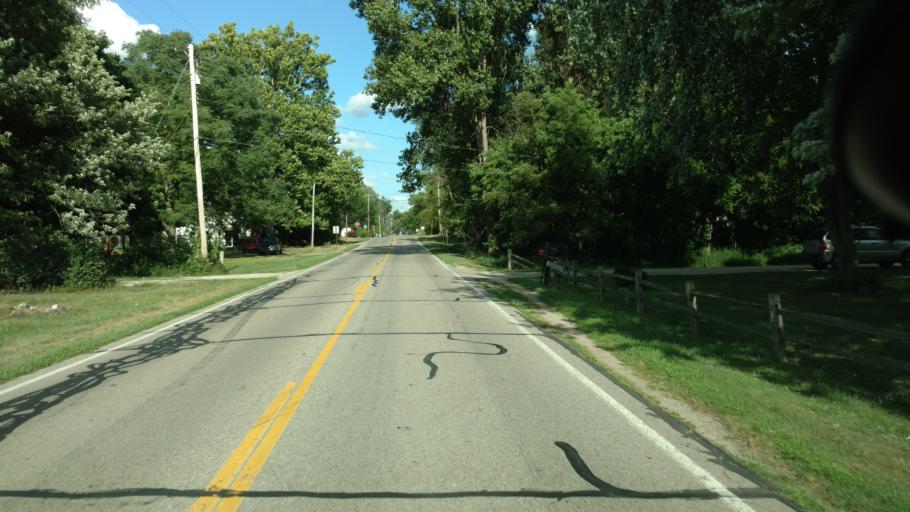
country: US
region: Michigan
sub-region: Ingham County
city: Lansing
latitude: 42.7842
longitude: -84.5579
